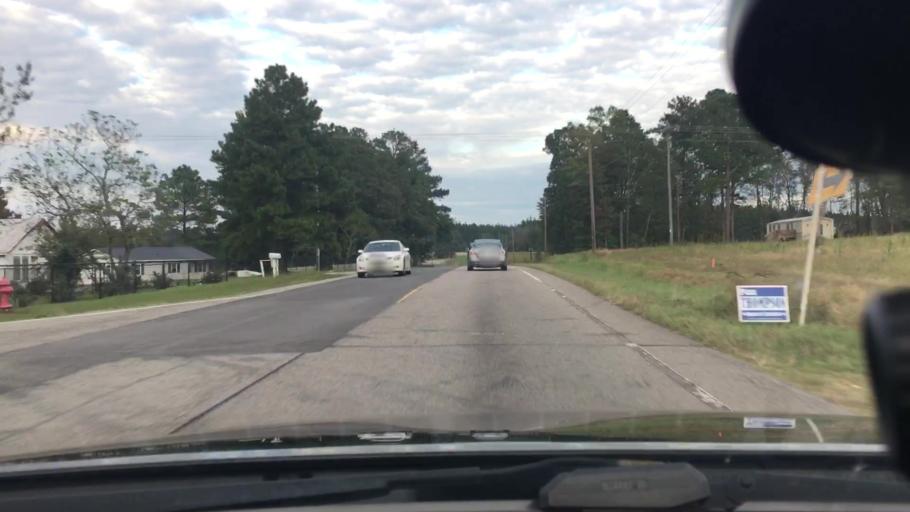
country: US
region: North Carolina
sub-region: Moore County
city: Carthage
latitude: 35.3603
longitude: -79.3261
